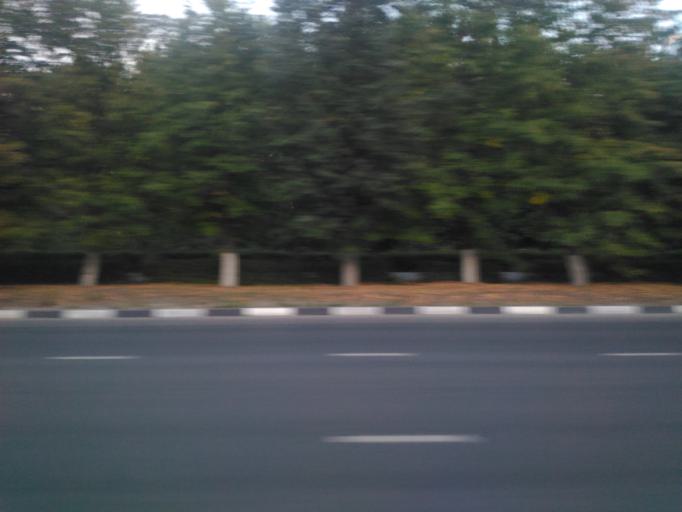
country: RU
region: Ulyanovsk
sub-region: Ulyanovskiy Rayon
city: Ulyanovsk
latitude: 54.2876
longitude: 48.3040
